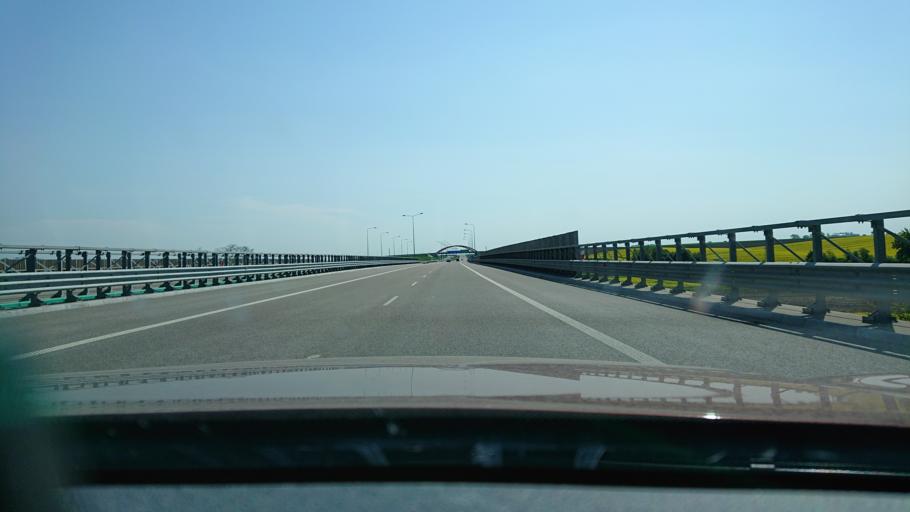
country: PL
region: Subcarpathian Voivodeship
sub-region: Powiat przemyski
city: Orly
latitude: 49.9136
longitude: 22.7964
